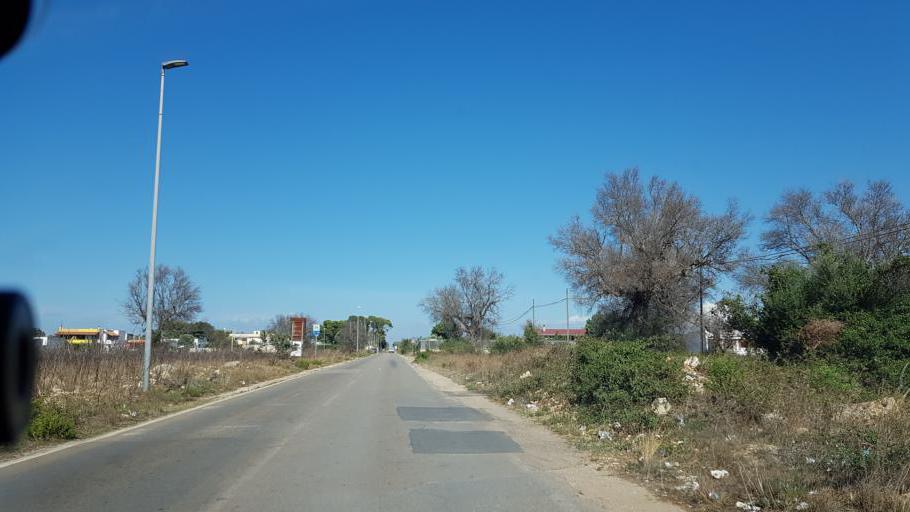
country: IT
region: Apulia
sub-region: Provincia di Lecce
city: Porto Cesareo
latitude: 40.2194
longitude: 17.9302
